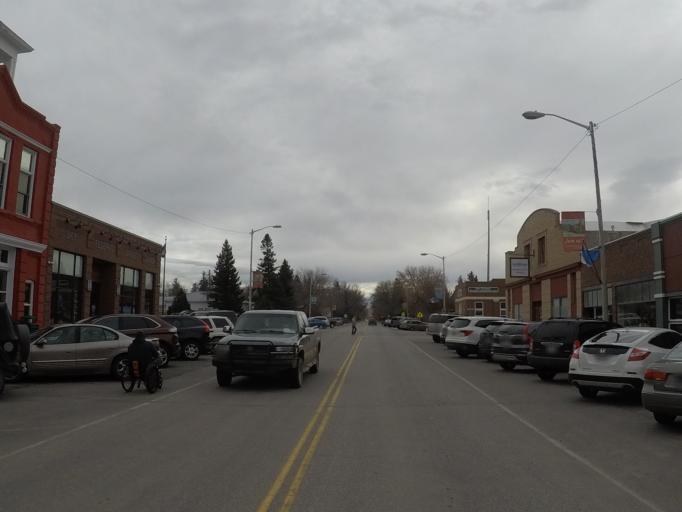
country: US
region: Montana
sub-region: Sweet Grass County
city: Big Timber
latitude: 45.8338
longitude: -109.9540
